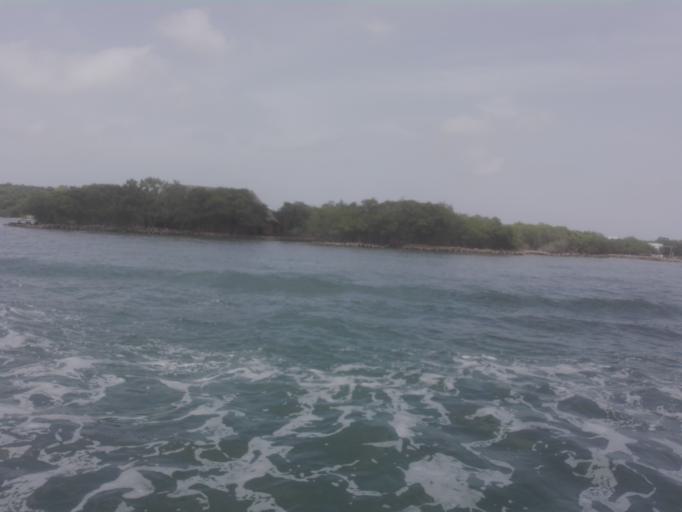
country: CO
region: Bolivar
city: Turbana
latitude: 10.1613
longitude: -75.6810
